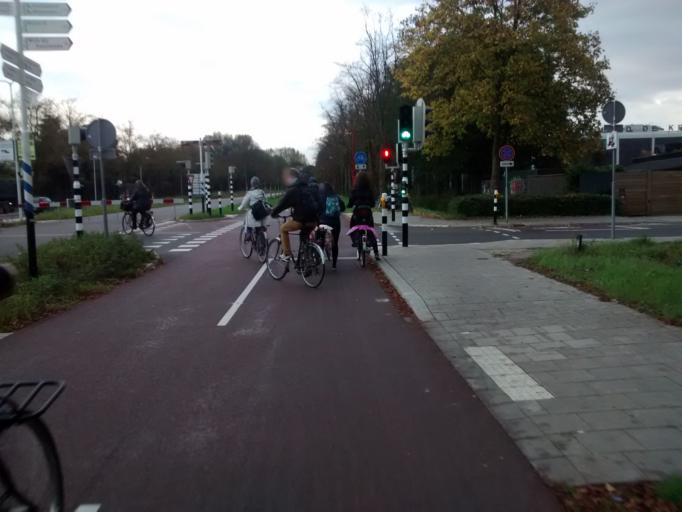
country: NL
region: Utrecht
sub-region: Gemeente Utrecht
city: Lunetten
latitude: 52.0824
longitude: 5.1560
